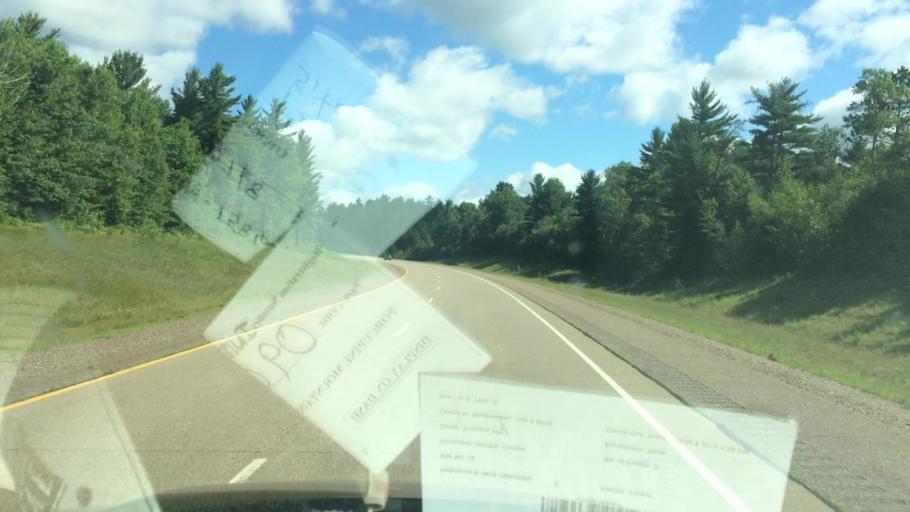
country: US
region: Wisconsin
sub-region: Lincoln County
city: Tomahawk
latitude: 45.5155
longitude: -89.6770
